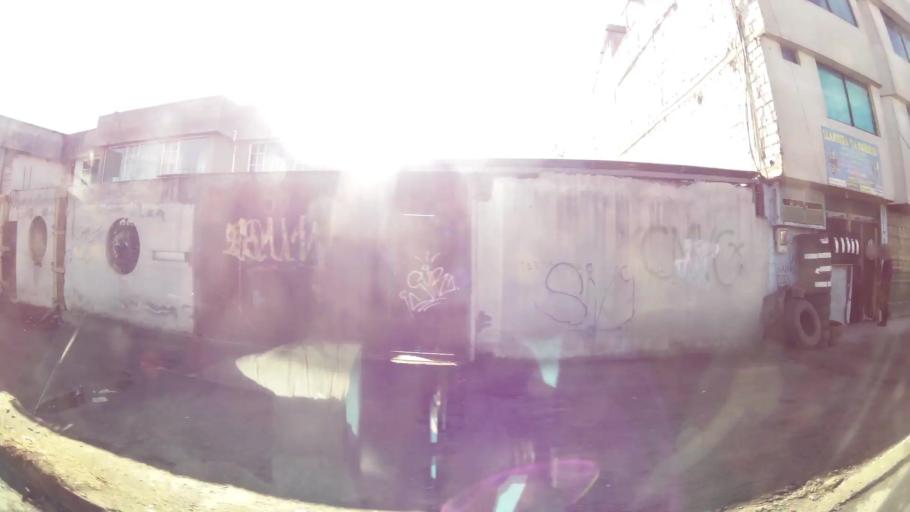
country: EC
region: Pichincha
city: Quito
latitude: -0.3176
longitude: -78.5577
